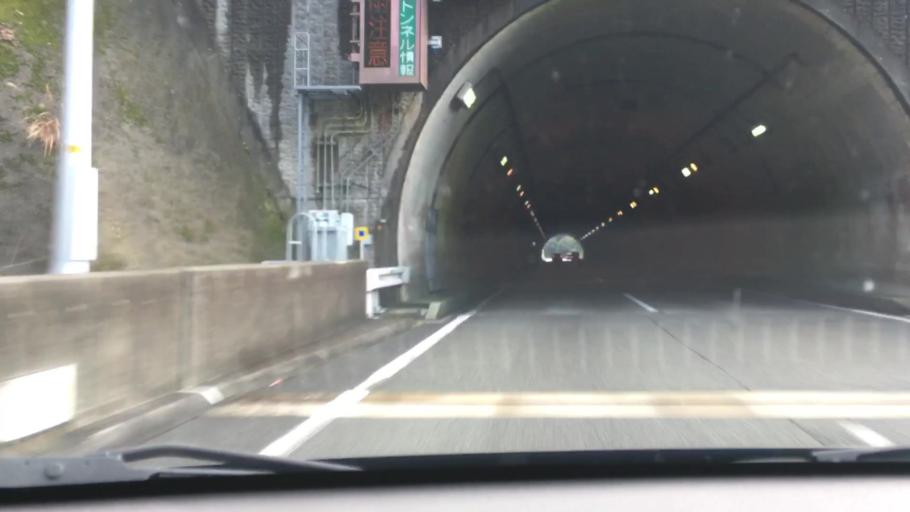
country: JP
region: Kumamoto
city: Yatsushiro
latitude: 32.4459
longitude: 130.6622
